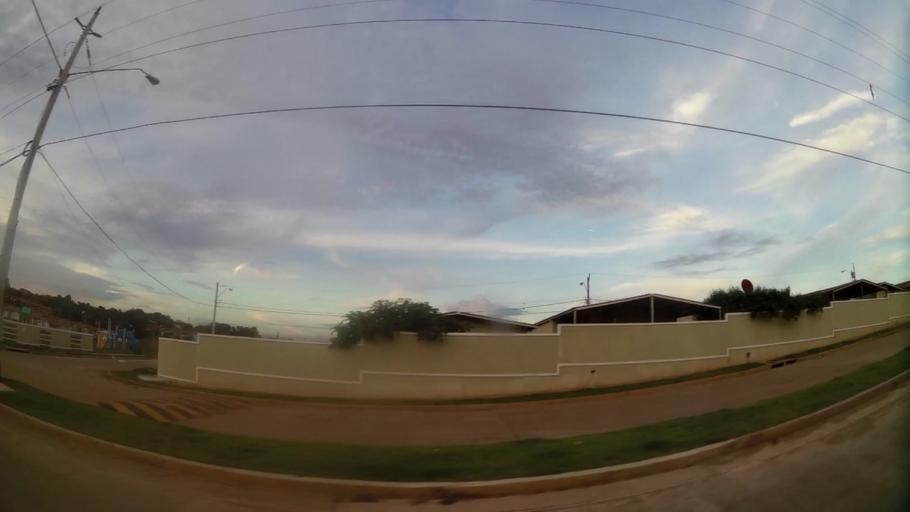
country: PA
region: Panama
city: La Mitra
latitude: 8.8577
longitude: -79.7604
